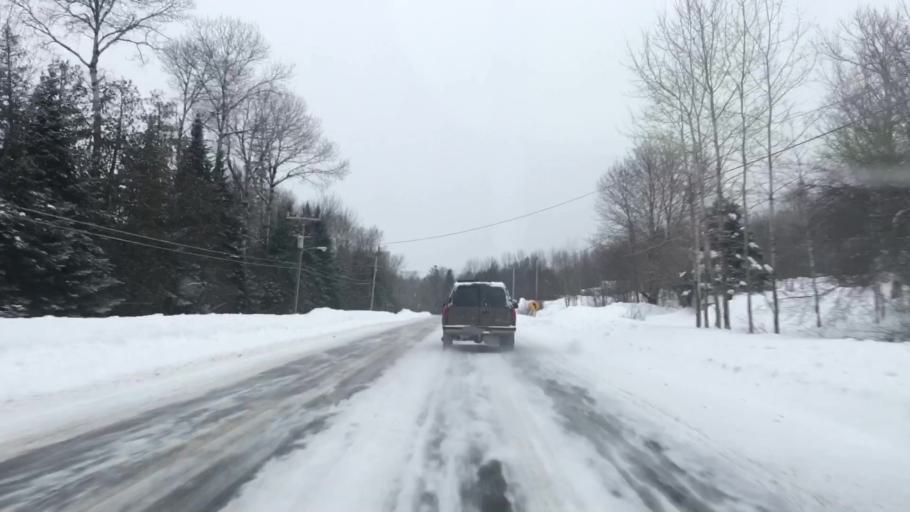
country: US
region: Maine
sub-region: Penobscot County
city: Medway
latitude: 45.5883
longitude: -68.4392
